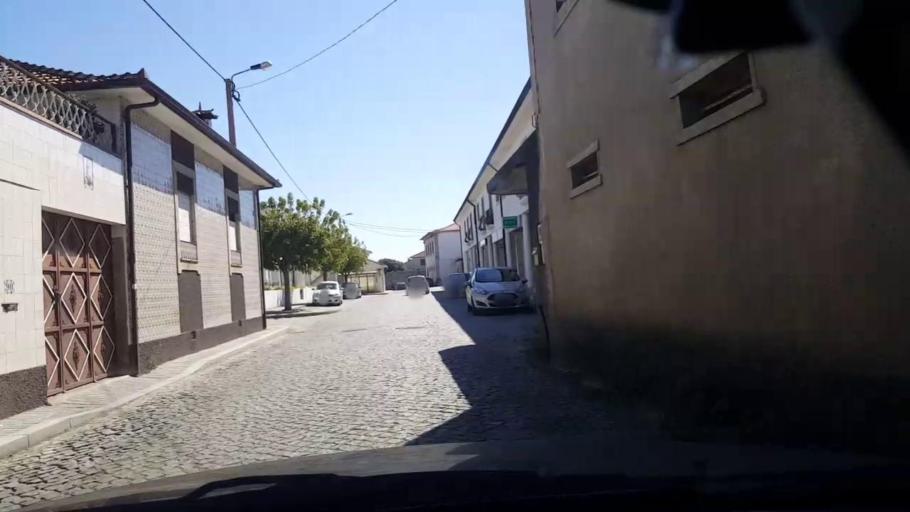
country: PT
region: Porto
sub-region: Vila do Conde
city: Arvore
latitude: 41.3146
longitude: -8.7208
